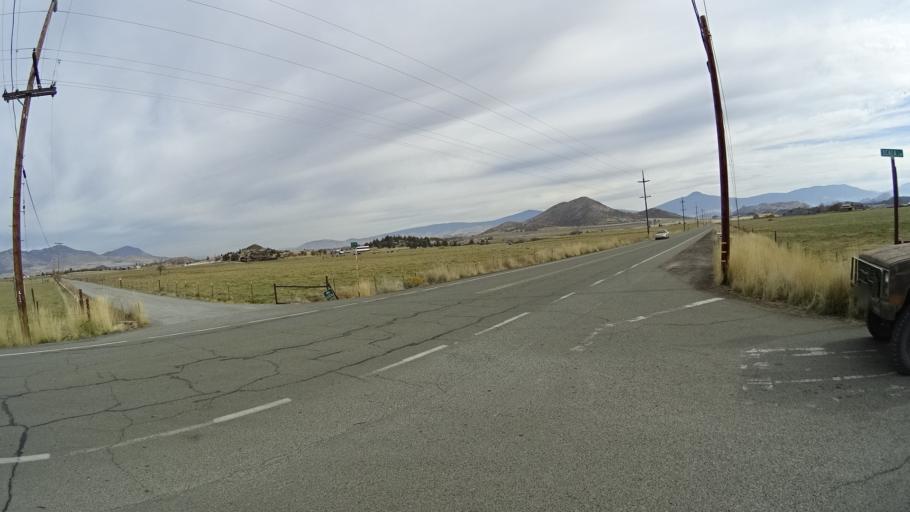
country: US
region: California
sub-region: Siskiyou County
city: Montague
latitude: 41.7068
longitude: -122.5494
